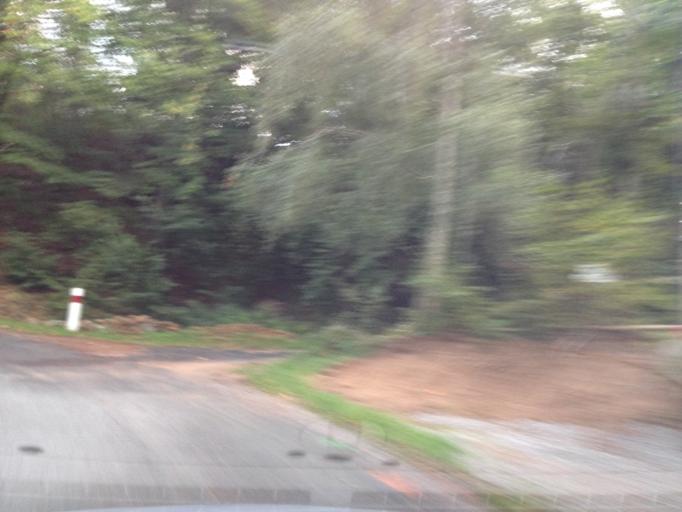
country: FR
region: Rhone-Alpes
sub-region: Departement de la Loire
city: Renaison
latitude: 46.0348
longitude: 3.8553
